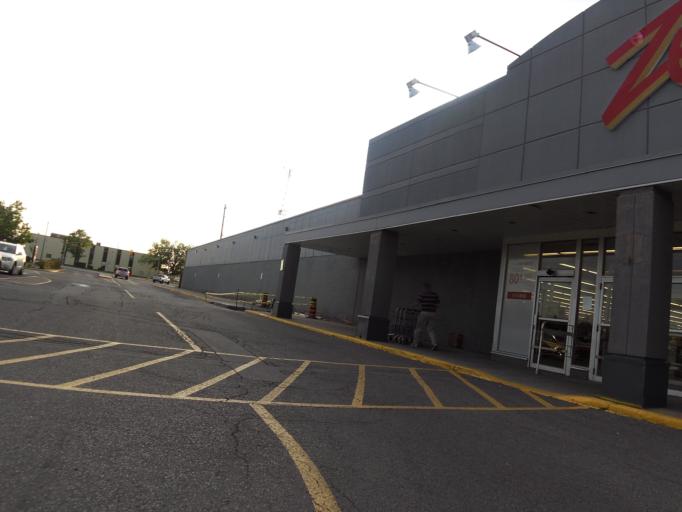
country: CA
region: Ontario
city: Bells Corners
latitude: 45.3242
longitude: -75.8330
